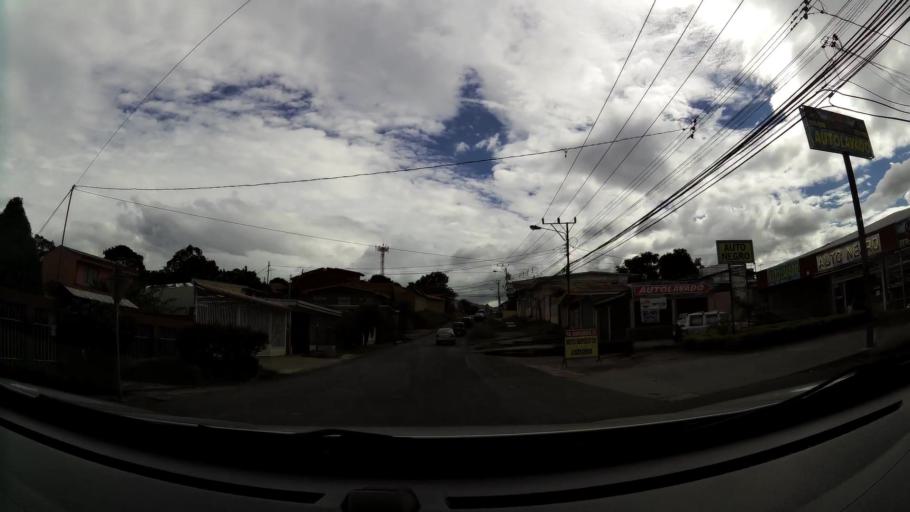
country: CR
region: San Jose
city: San Rafael Arriba
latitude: 9.8872
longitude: -84.0777
